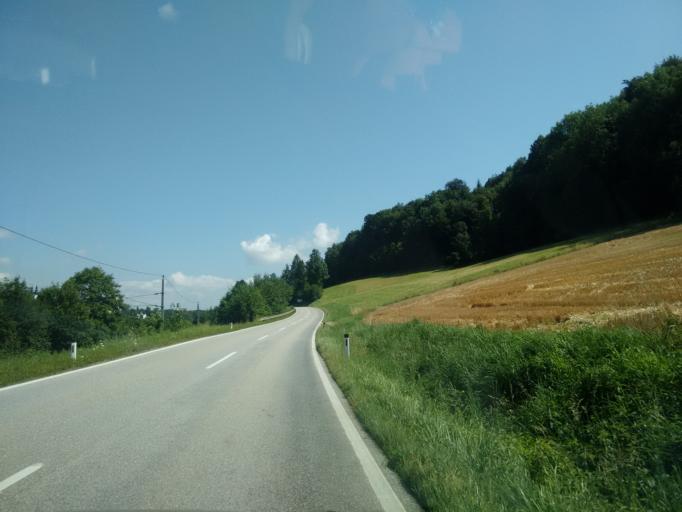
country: AT
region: Upper Austria
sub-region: Politischer Bezirk Kirchdorf an der Krems
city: Kremsmunster
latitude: 48.0439
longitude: 14.1278
